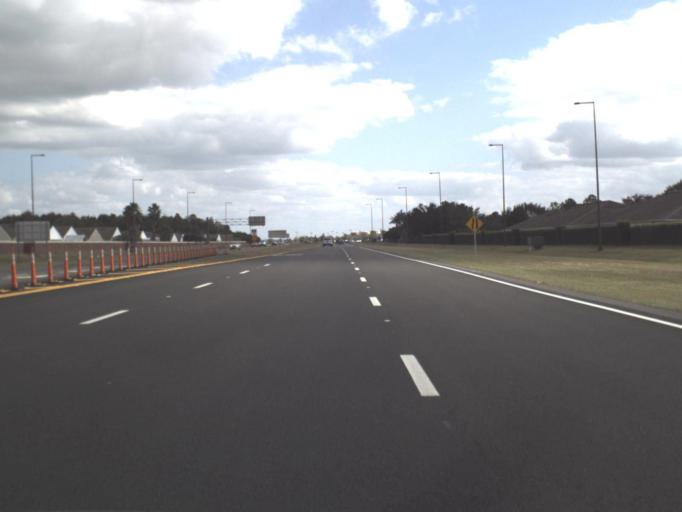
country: US
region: Florida
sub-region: Orange County
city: Hunters Creek
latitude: 28.3445
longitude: -81.4390
